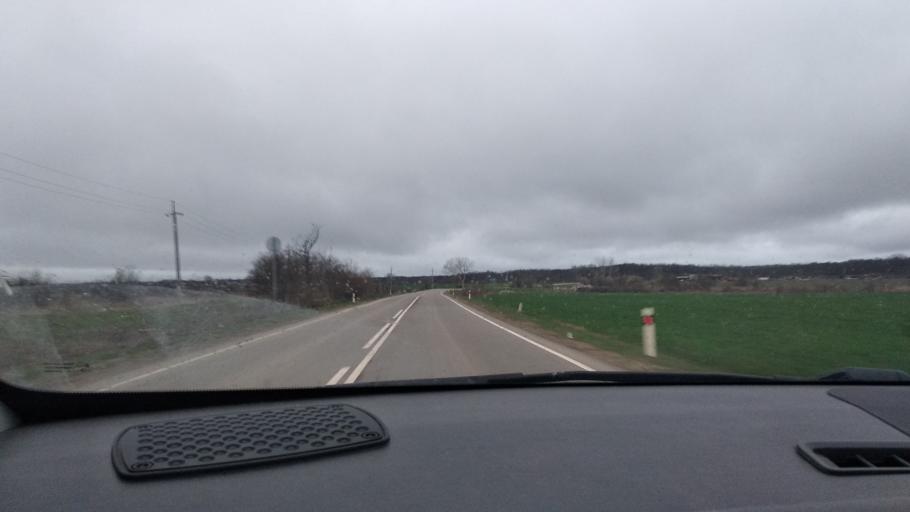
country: RU
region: Krasnodarskiy
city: Afipskiy
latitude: 44.8994
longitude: 38.7794
